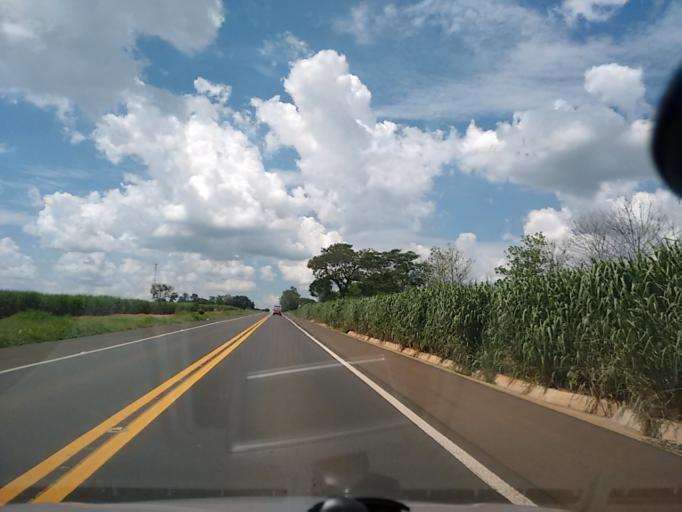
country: BR
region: Sao Paulo
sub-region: Osvaldo Cruz
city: Osvaldo Cruz
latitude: -21.9228
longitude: -50.9022
